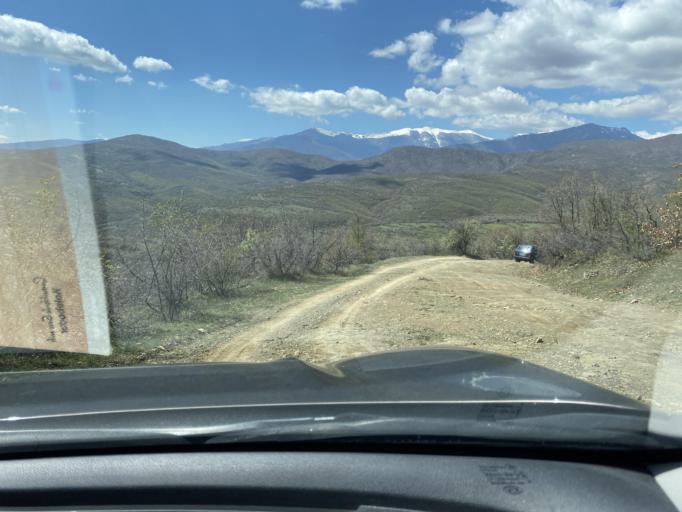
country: MK
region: Caska
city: Caska
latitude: 41.7312
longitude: 21.6555
